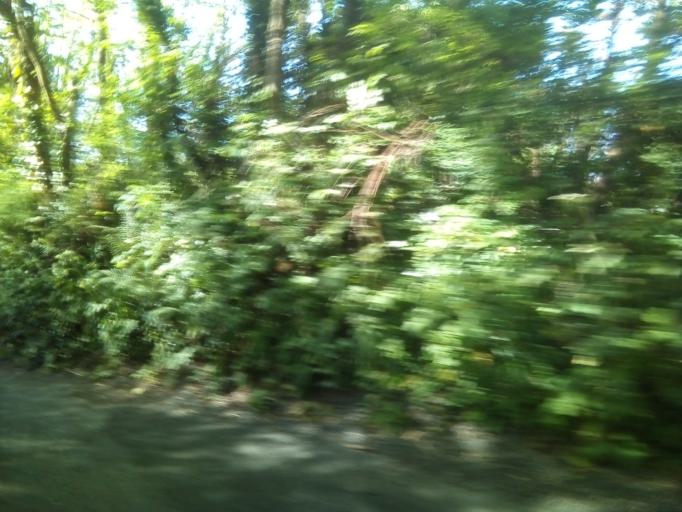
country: IE
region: Leinster
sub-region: Loch Garman
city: Loch Garman
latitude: 52.2237
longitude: -6.5439
